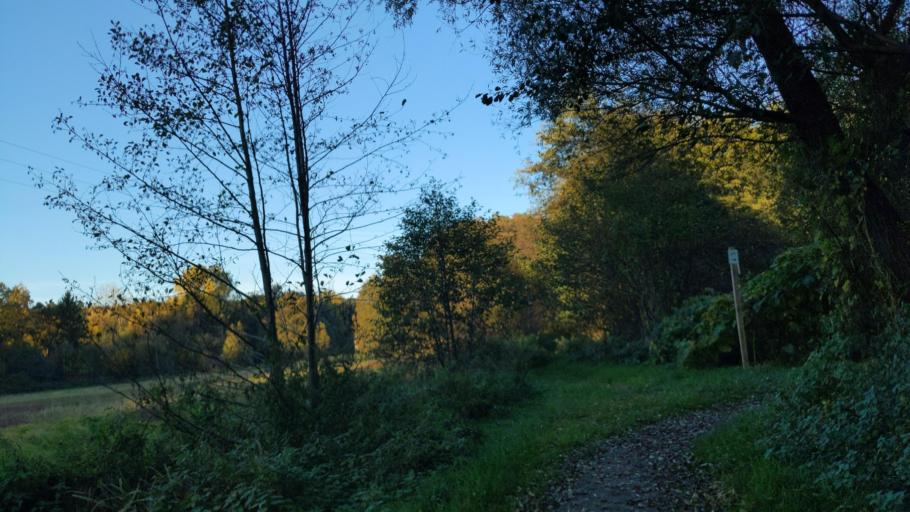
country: DE
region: Schleswig-Holstein
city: Gross Gronau
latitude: 53.7807
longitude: 10.7571
